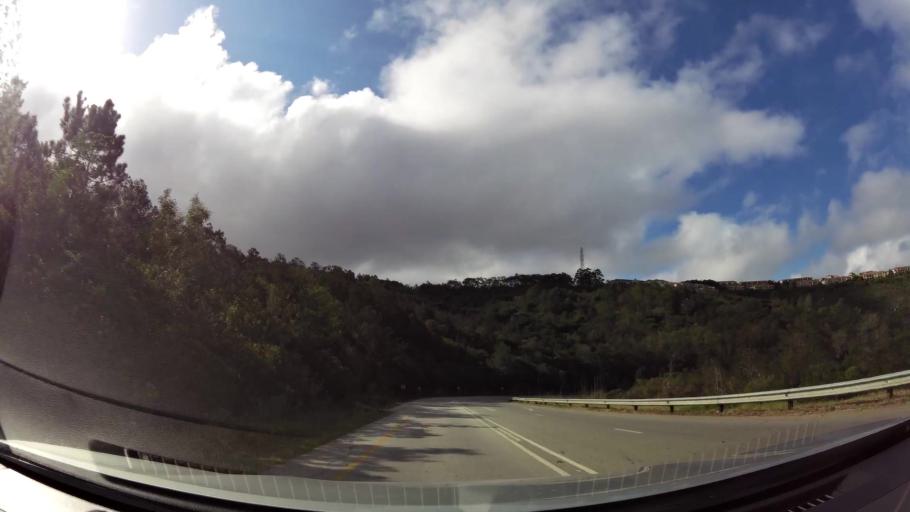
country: ZA
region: Western Cape
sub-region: Eden District Municipality
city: Plettenberg Bay
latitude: -34.0553
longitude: 23.3530
